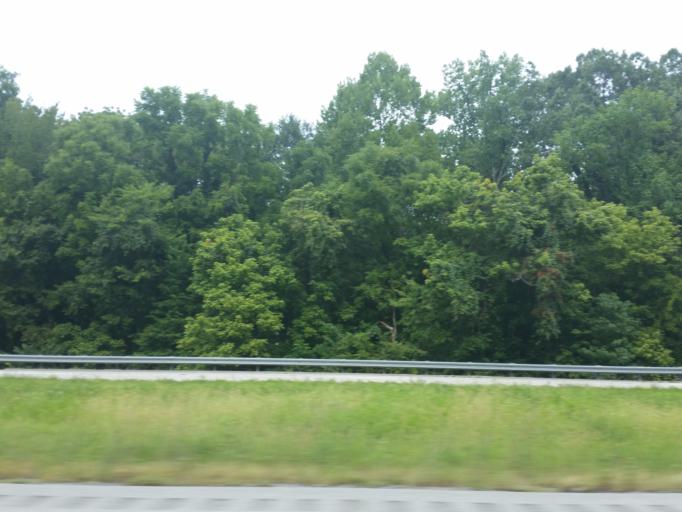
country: US
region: Kentucky
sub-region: Lyon County
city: Eddyville
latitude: 37.0385
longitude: -88.0093
